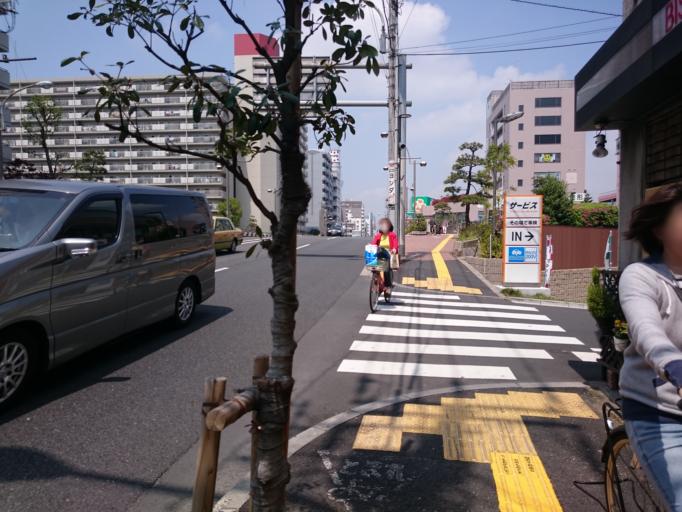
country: JP
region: Tokyo
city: Urayasu
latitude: 35.6841
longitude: 139.8161
